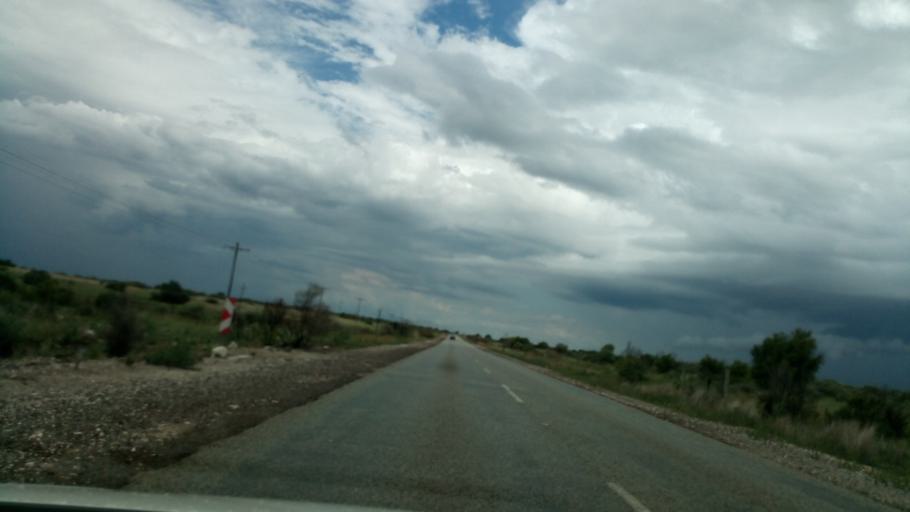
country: ZA
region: Northern Cape
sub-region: Siyanda District Municipality
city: Danielskuil
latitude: -28.2561
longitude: 24.0495
